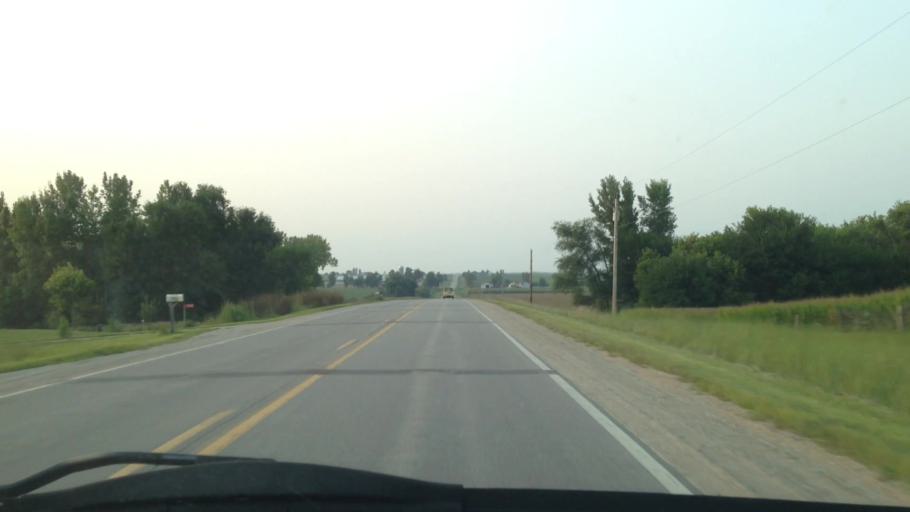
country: US
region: Iowa
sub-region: Benton County
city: Atkins
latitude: 41.9973
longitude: -91.8734
